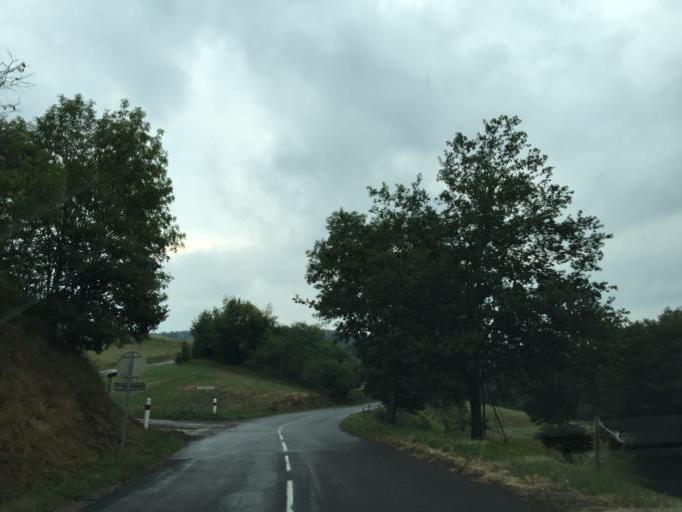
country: FR
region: Rhone-Alpes
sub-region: Departement de la Loire
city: Saint-Christo-en-Jarez
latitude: 45.5240
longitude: 4.4541
